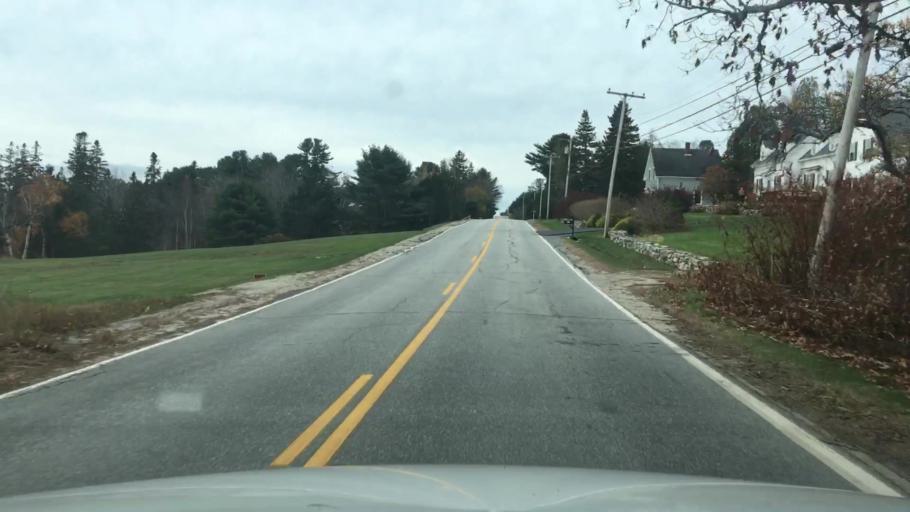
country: US
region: Maine
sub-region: Hancock County
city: Sedgwick
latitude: 44.3481
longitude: -68.5540
